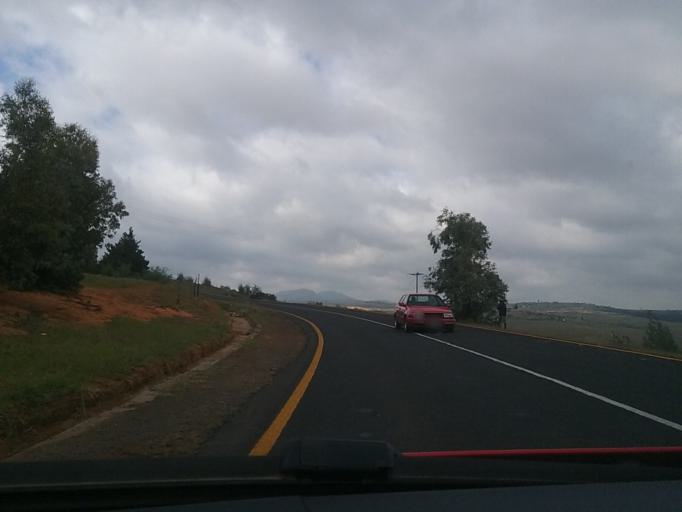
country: LS
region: Berea
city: Teyateyaneng
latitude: -29.1822
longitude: 27.7876
